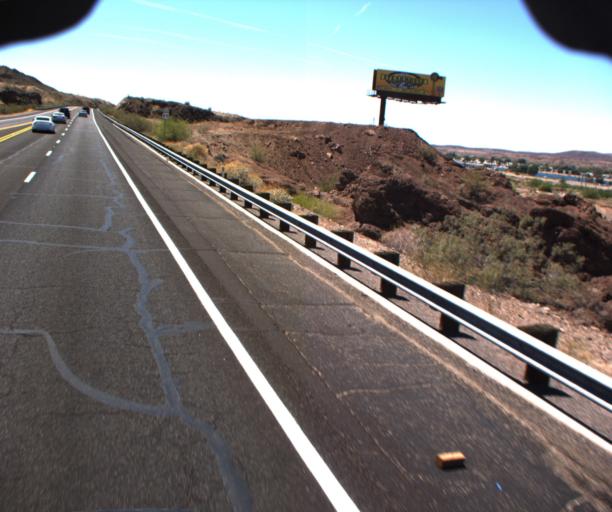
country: US
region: Arizona
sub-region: La Paz County
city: Cienega Springs
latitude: 34.2159
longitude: -114.1957
